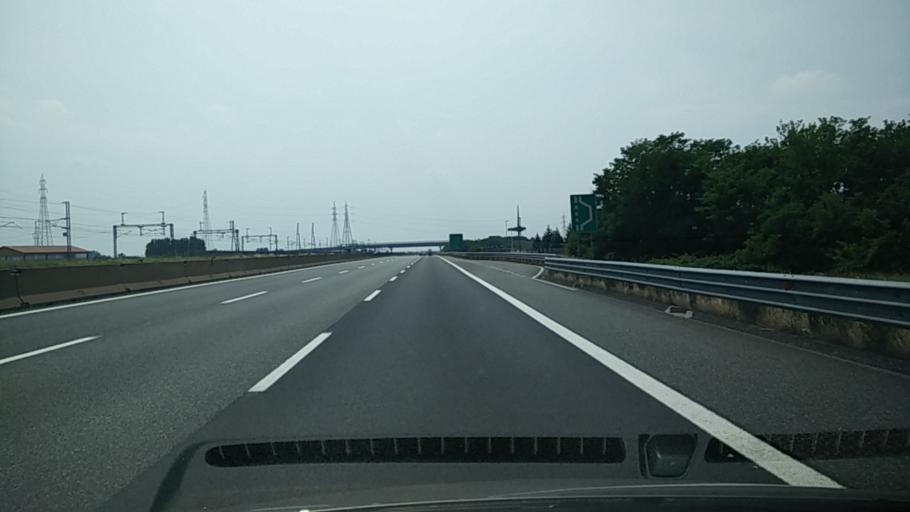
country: IT
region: Lombardy
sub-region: Citta metropolitana di Milano
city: Casate
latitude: 45.4833
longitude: 8.8461
